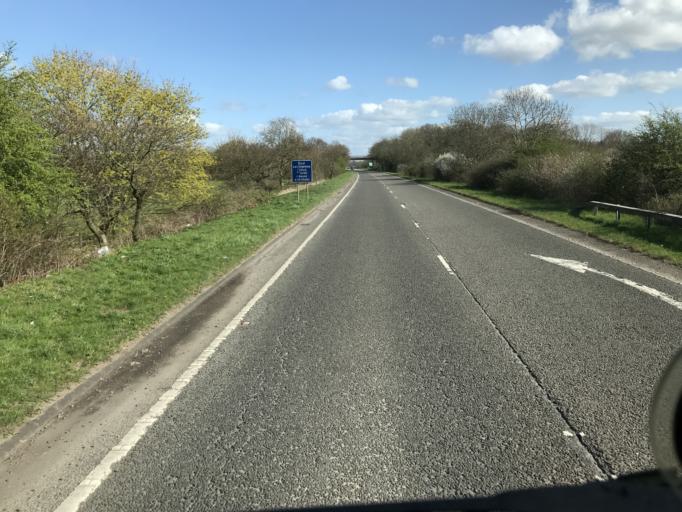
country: GB
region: Wales
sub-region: County of Flintshire
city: Hawarden
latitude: 53.1650
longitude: -2.9734
